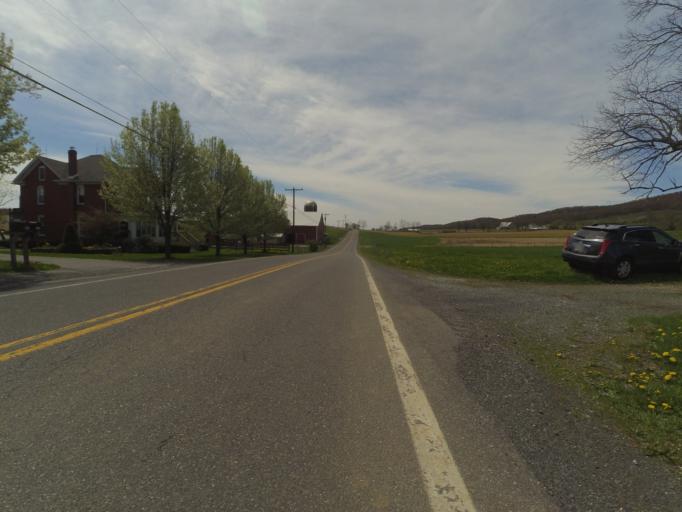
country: US
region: Pennsylvania
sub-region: Centre County
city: Stormstown
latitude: 40.7539
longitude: -78.0707
